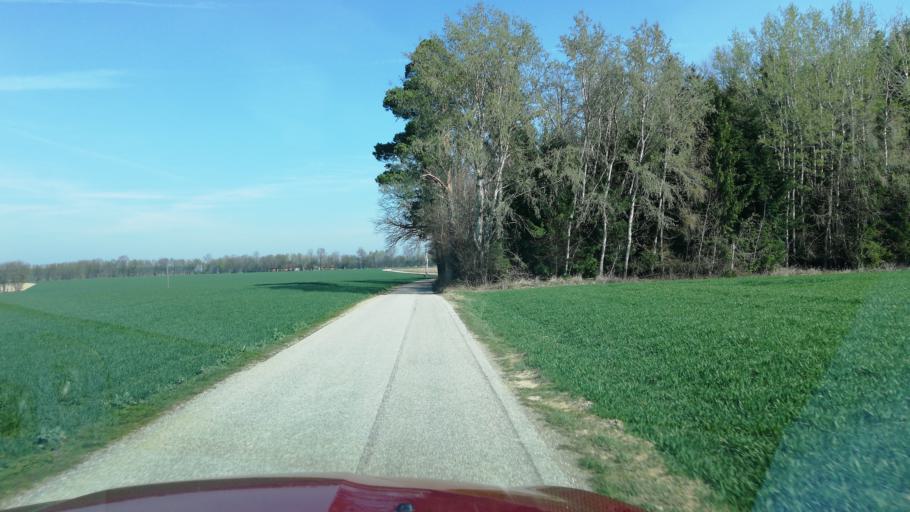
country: AT
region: Upper Austria
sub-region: Wels-Land
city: Sattledt
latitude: 48.1129
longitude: 14.0720
